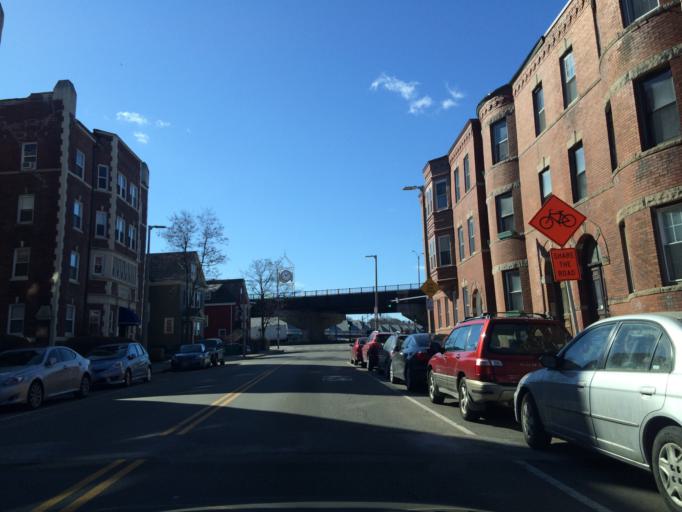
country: US
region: Massachusetts
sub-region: Suffolk County
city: Jamaica Plain
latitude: 42.3029
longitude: -71.1146
